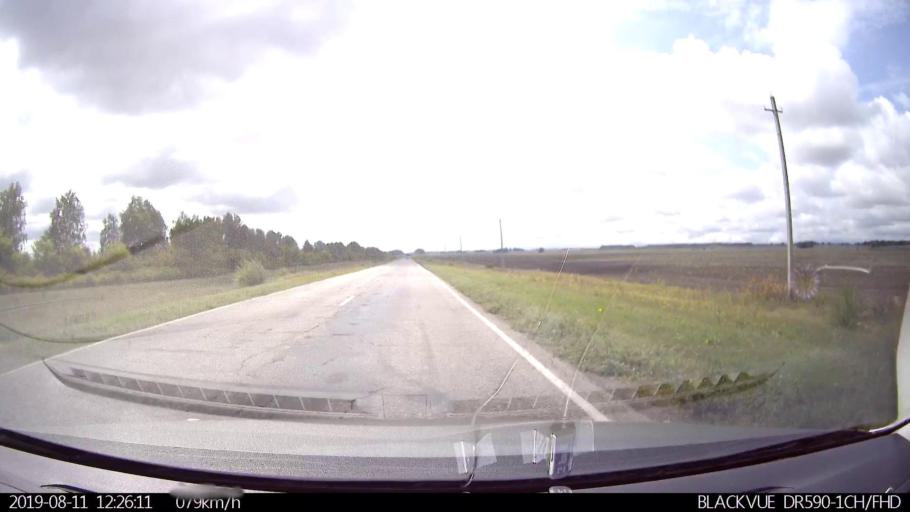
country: RU
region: Ulyanovsk
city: Ignatovka
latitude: 53.8664
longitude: 47.9321
